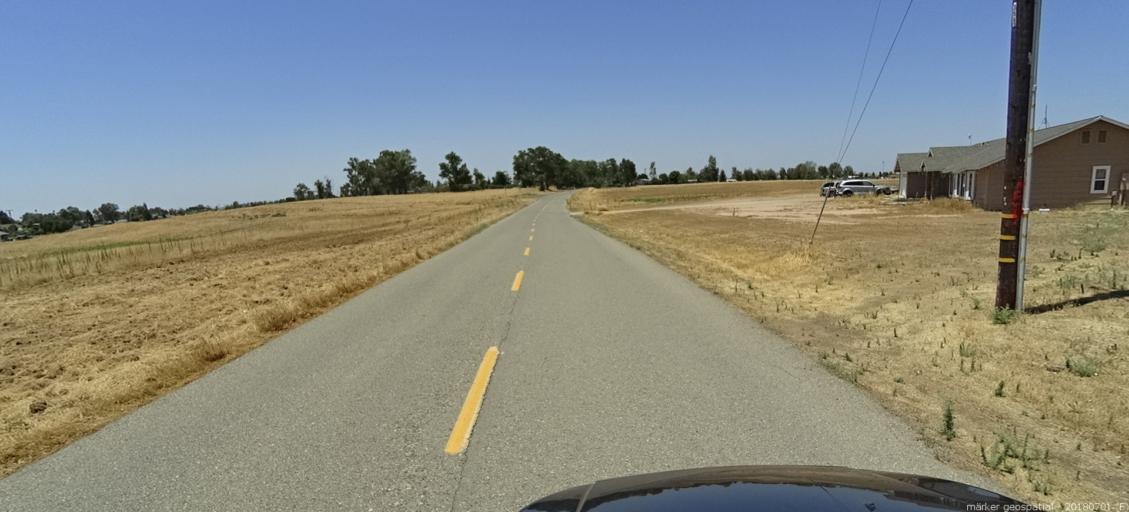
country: US
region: California
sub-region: Madera County
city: Madera Acres
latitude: 37.0529
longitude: -119.9856
